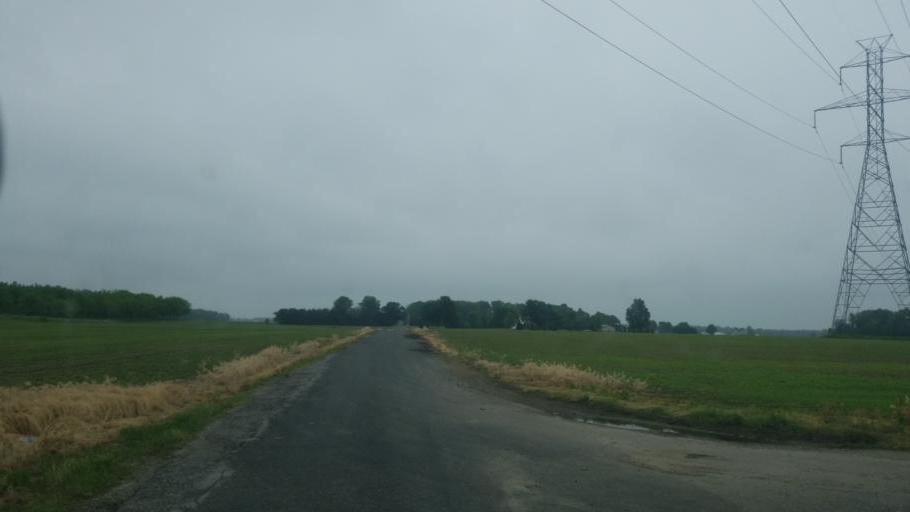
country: US
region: Indiana
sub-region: Marshall County
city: Bremen
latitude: 41.4794
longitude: -86.1274
